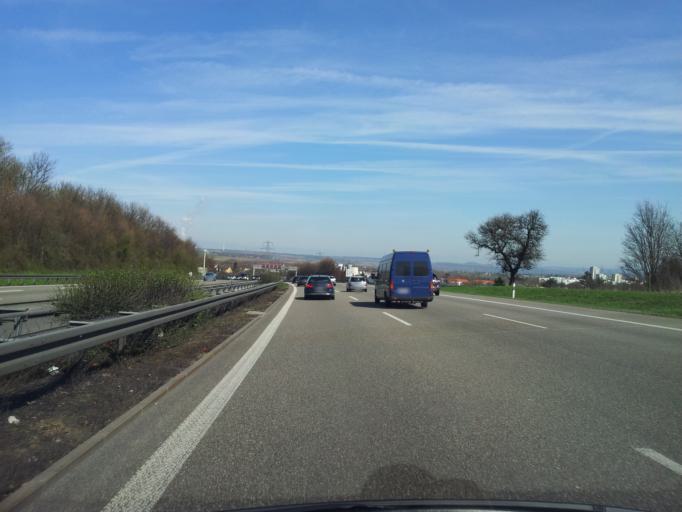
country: DE
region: Baden-Wuerttemberg
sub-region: Regierungsbezirk Stuttgart
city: Asperg
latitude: 48.9002
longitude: 9.1535
